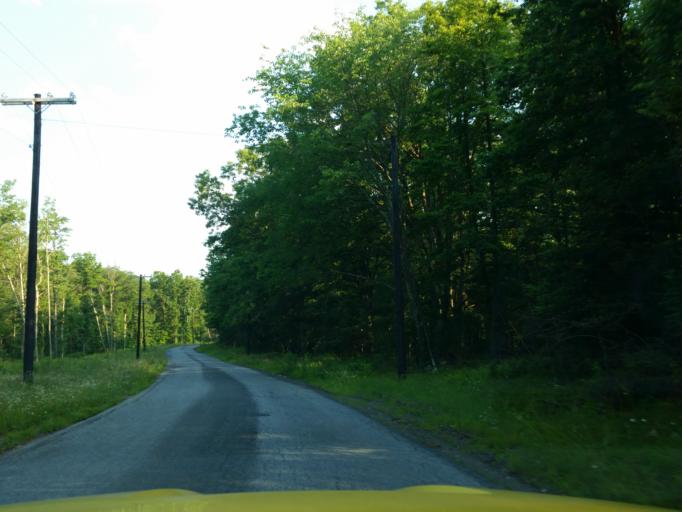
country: US
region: Pennsylvania
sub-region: Dauphin County
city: Williamstown
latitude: 40.4561
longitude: -76.6274
